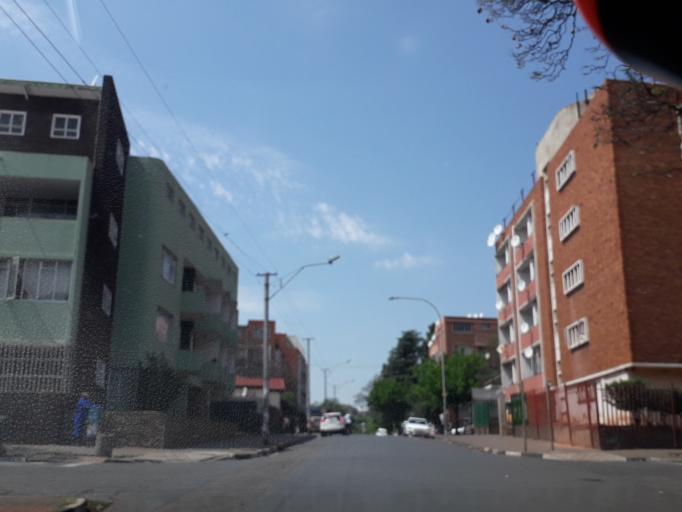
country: ZA
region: Gauteng
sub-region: City of Johannesburg Metropolitan Municipality
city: Johannesburg
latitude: -26.1768
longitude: 28.0665
